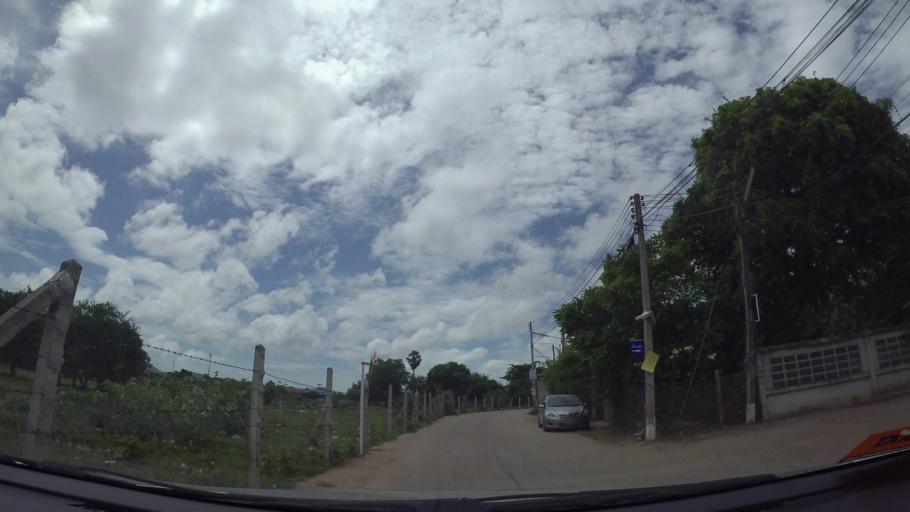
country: TH
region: Chon Buri
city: Sattahip
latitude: 12.6762
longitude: 100.8997
